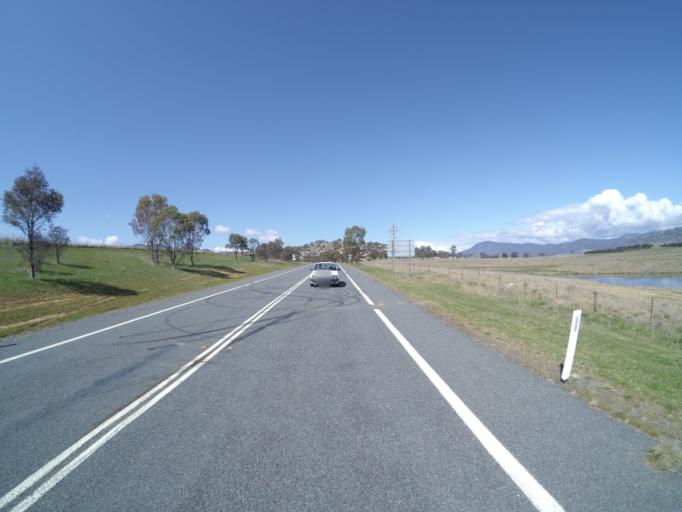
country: AU
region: Australian Capital Territory
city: Macarthur
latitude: -35.4541
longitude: 149.0758
